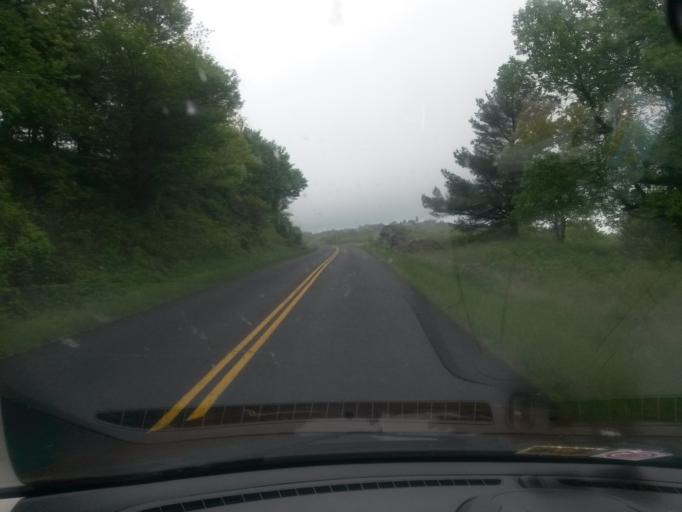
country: US
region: Virginia
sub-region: Floyd County
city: Floyd
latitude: 36.8044
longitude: -80.3628
